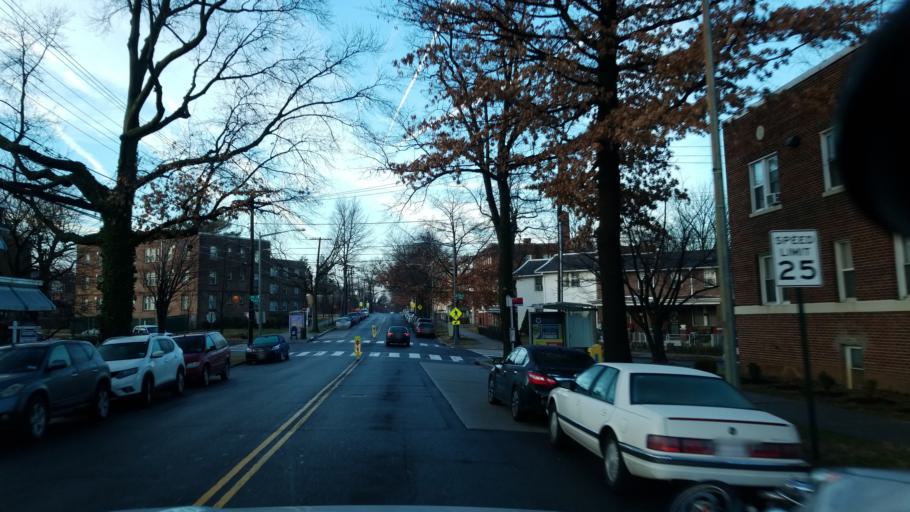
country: US
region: Maryland
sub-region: Prince George's County
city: Hillcrest Heights
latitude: 38.8704
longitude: -76.9769
